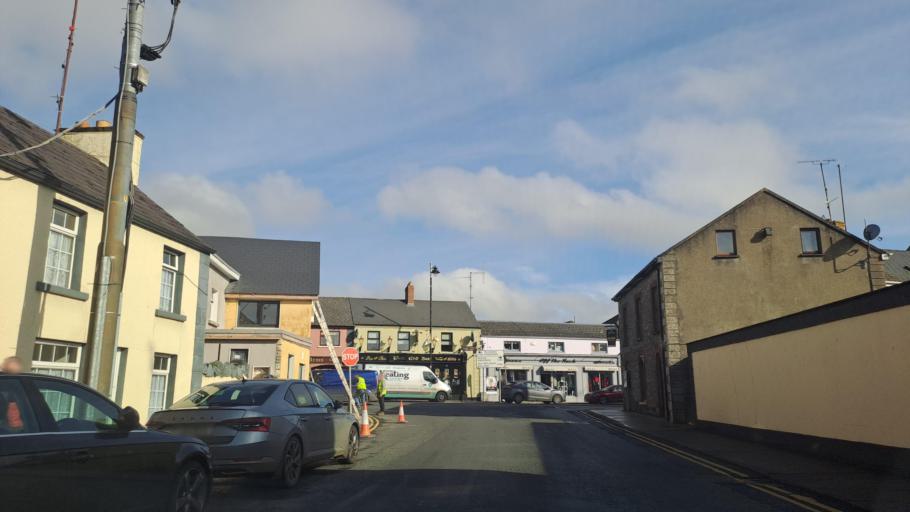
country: IE
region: Ulster
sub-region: An Cabhan
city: Cootehill
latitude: 54.0727
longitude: -7.0838
